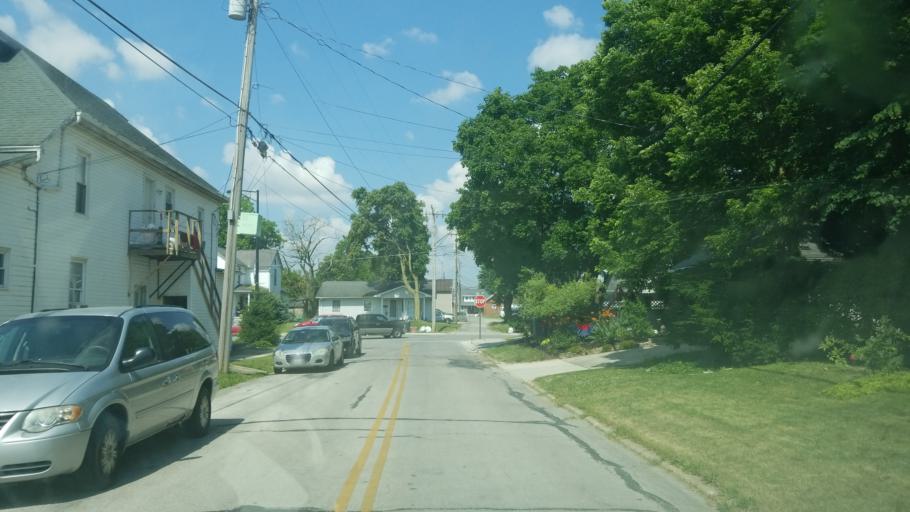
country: US
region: Ohio
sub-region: Auglaize County
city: Wapakoneta
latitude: 40.5699
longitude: -84.1877
